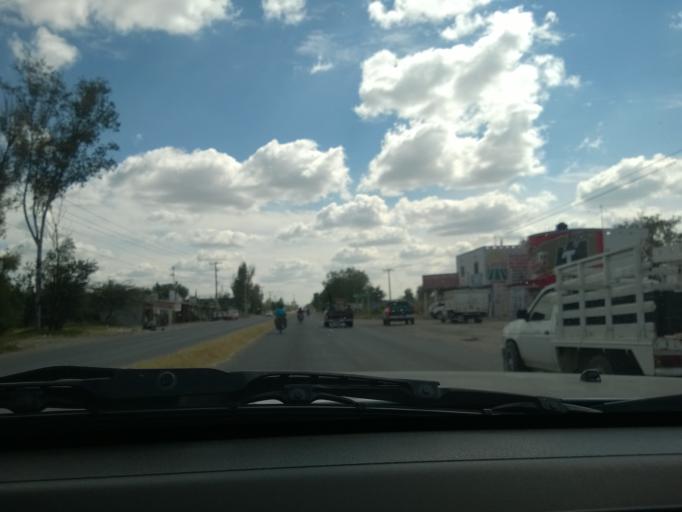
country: MX
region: Guanajuato
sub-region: Leon
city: El CERESO
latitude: 20.9954
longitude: -101.7030
